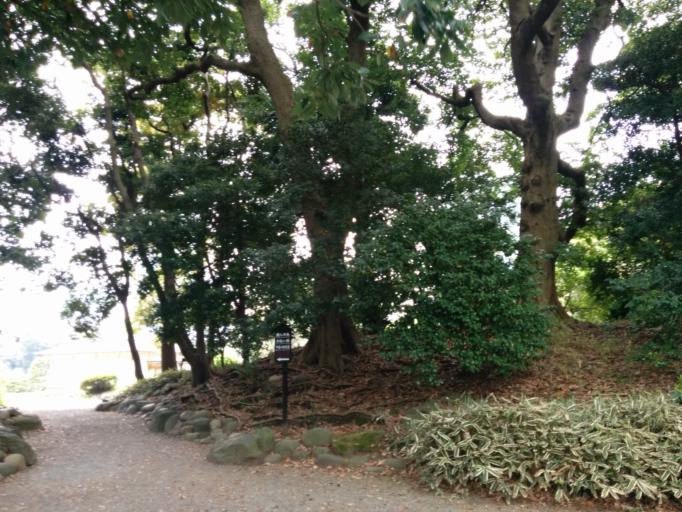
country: JP
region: Tokyo
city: Tokyo
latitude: 35.6599
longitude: 139.7626
